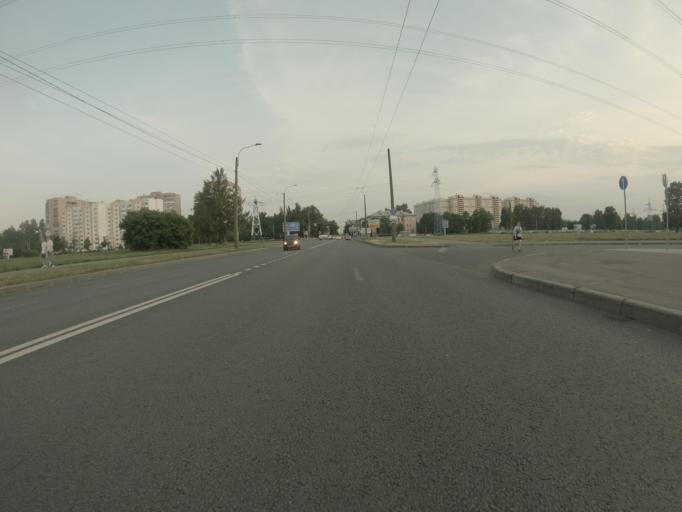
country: RU
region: Leningrad
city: Kalininskiy
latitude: 59.9788
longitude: 30.3940
